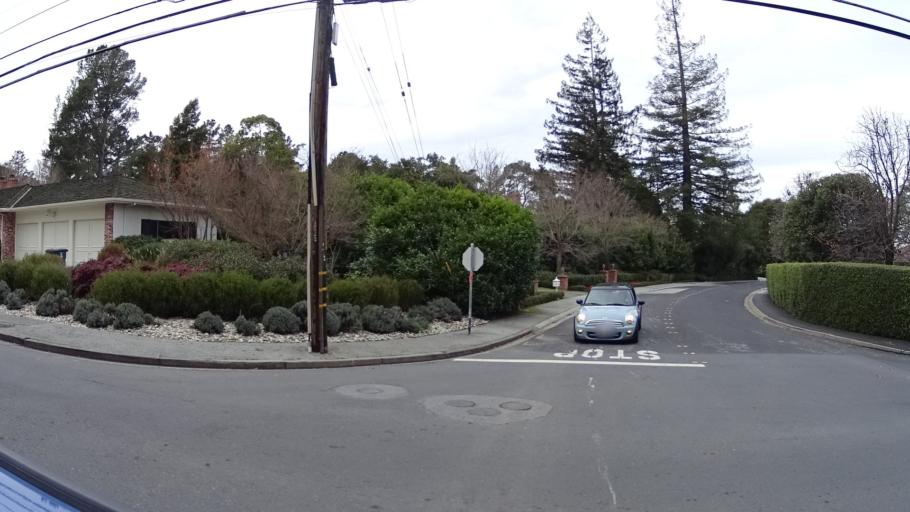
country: US
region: California
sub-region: San Mateo County
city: Burlingame
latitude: 37.5714
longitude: -122.3566
